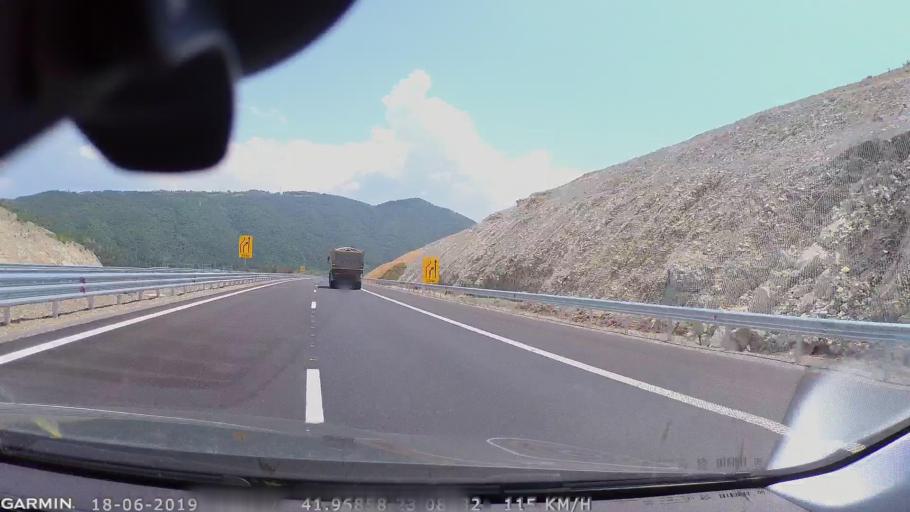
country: BG
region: Blagoevgrad
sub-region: Obshtina Blagoevgrad
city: Blagoevgrad
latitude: 41.9677
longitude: 23.0901
